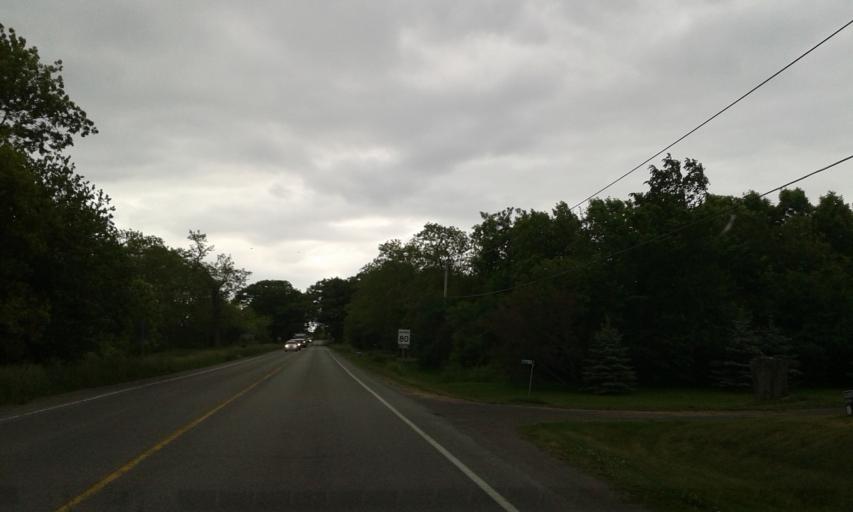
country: CA
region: Ontario
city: Prince Edward
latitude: 43.9448
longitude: -77.4225
